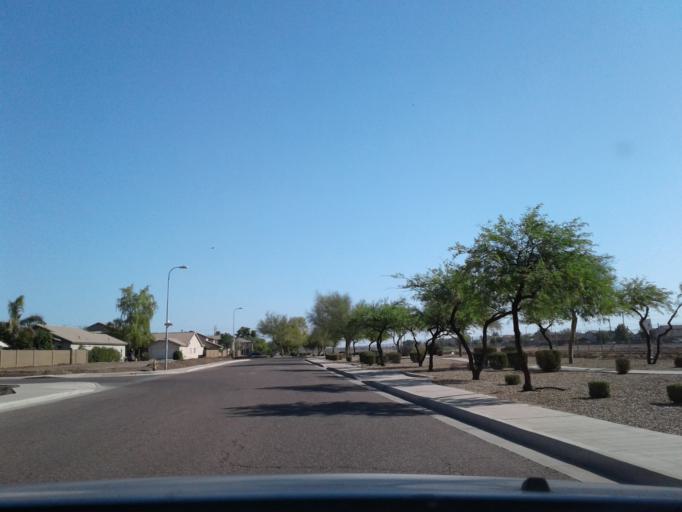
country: US
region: Arizona
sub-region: Maricopa County
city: Laveen
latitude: 33.4094
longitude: -112.1925
